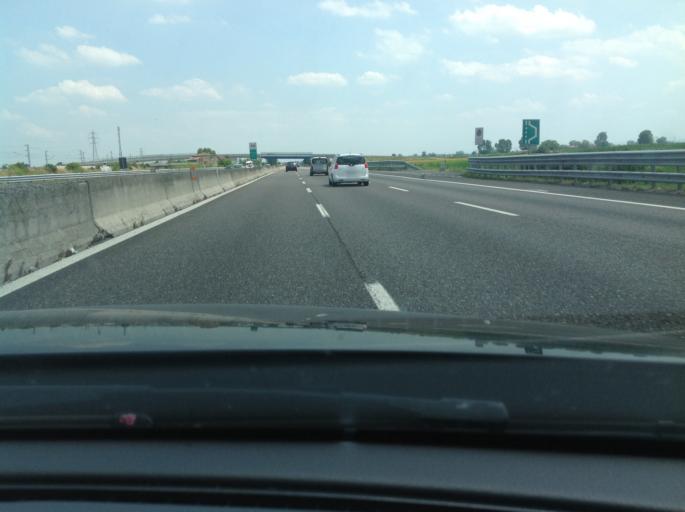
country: IT
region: Emilia-Romagna
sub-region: Provincia di Piacenza
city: Roveleto
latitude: 44.9784
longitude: 9.8683
